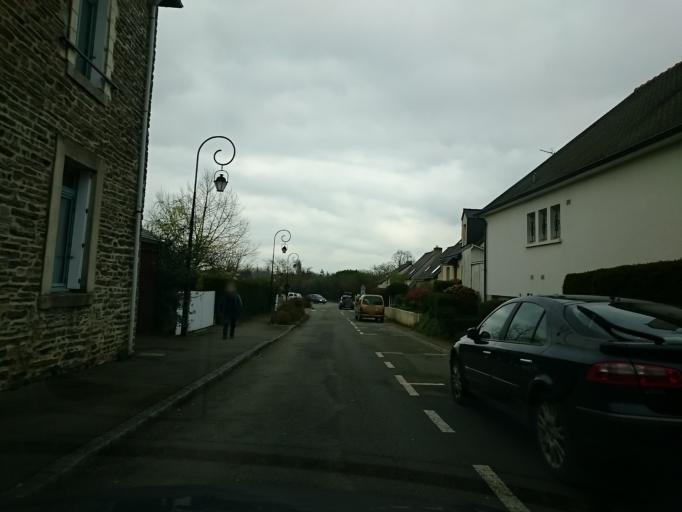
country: FR
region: Brittany
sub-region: Departement d'Ille-et-Vilaine
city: Corps-Nuds
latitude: 47.9783
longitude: -1.5866
